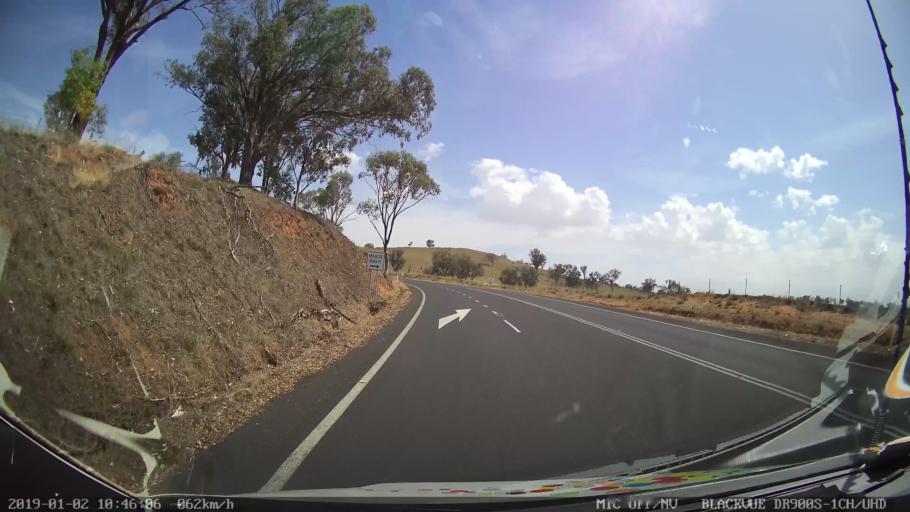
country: AU
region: New South Wales
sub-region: Cootamundra
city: Cootamundra
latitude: -34.7541
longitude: 148.2895
